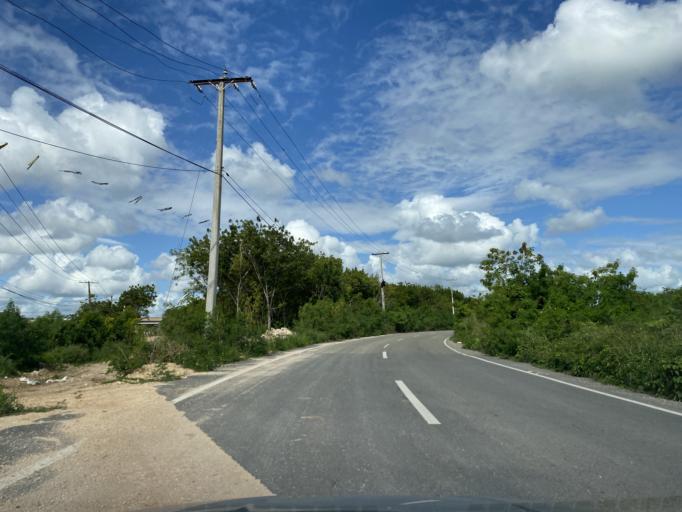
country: DO
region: Santo Domingo
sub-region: Santo Domingo
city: Boca Chica
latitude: 18.4495
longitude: -69.5935
